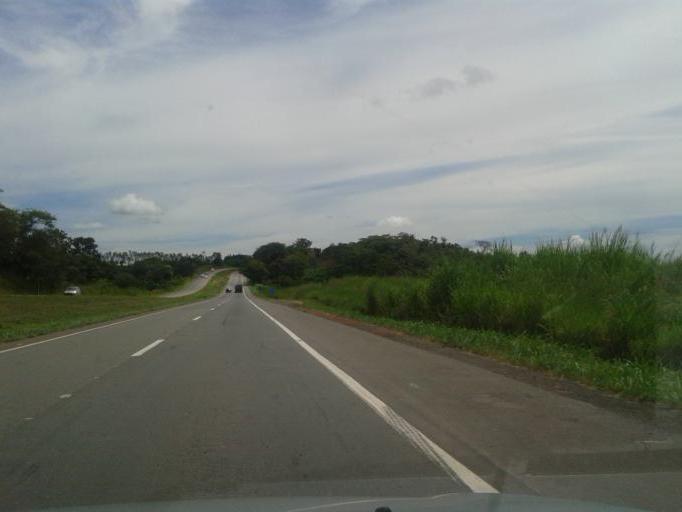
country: BR
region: Goias
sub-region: Hidrolandia
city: Hidrolandia
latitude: -17.1424
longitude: -49.2152
